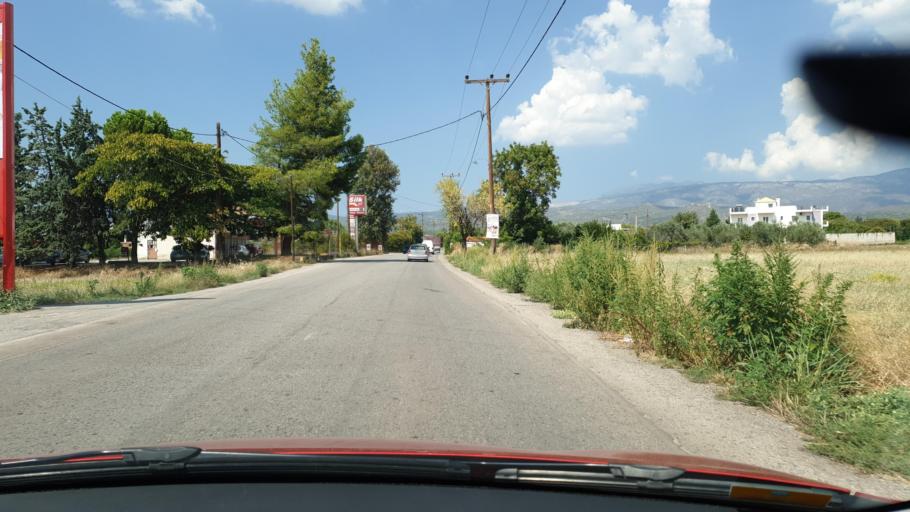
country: GR
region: Central Greece
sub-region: Nomos Evvoias
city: Kastella
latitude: 38.5627
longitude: 23.6316
